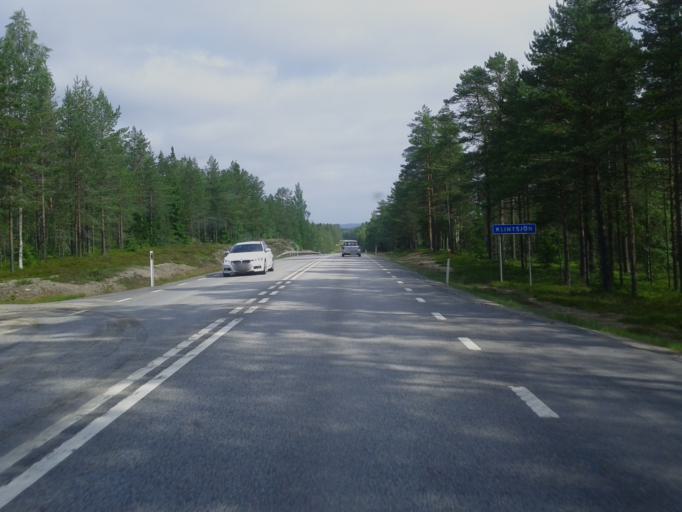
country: SE
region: Vaesterbotten
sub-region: Robertsfors Kommun
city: Robertsfors
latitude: 64.1962
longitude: 21.0068
